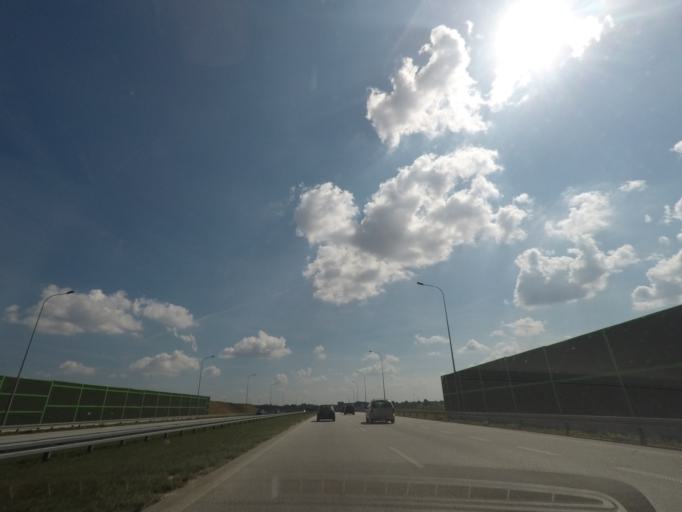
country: PL
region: Lodz Voivodeship
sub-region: Powiat zgierski
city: Strykow
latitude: 51.8455
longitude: 19.6597
